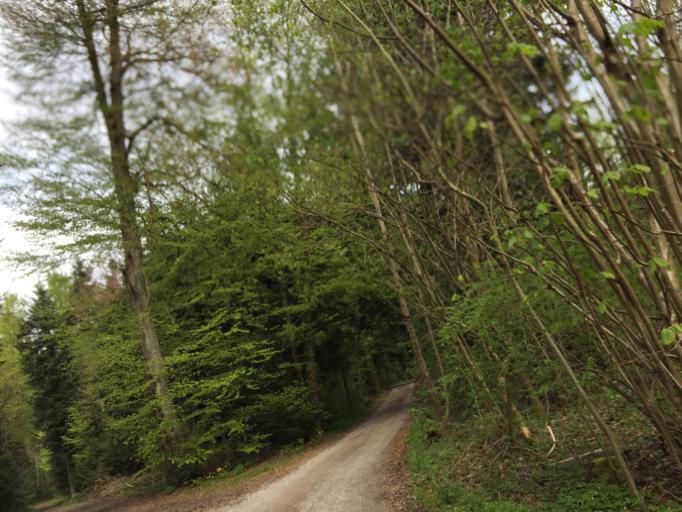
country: CH
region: Bern
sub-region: Bern-Mittelland District
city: Rubigen
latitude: 46.9223
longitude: 7.5343
